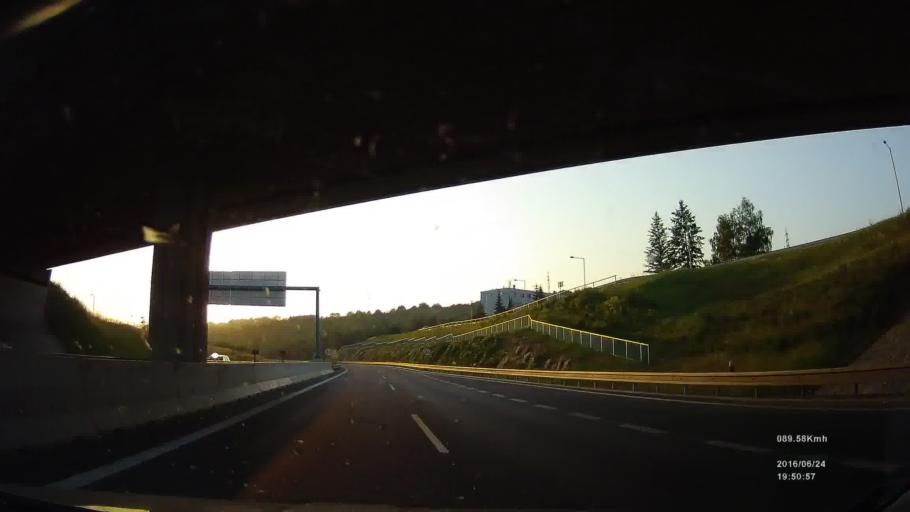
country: SK
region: Banskobystricky
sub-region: Okres Banska Bystrica
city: Banska Bystrica
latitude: 48.7416
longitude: 19.1814
